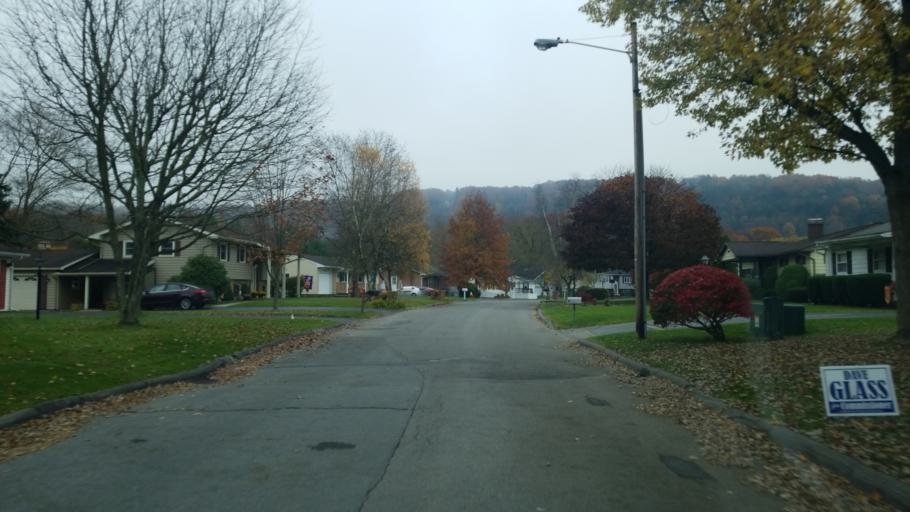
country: US
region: Pennsylvania
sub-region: Clearfield County
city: Clearfield
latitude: 41.0078
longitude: -78.4384
